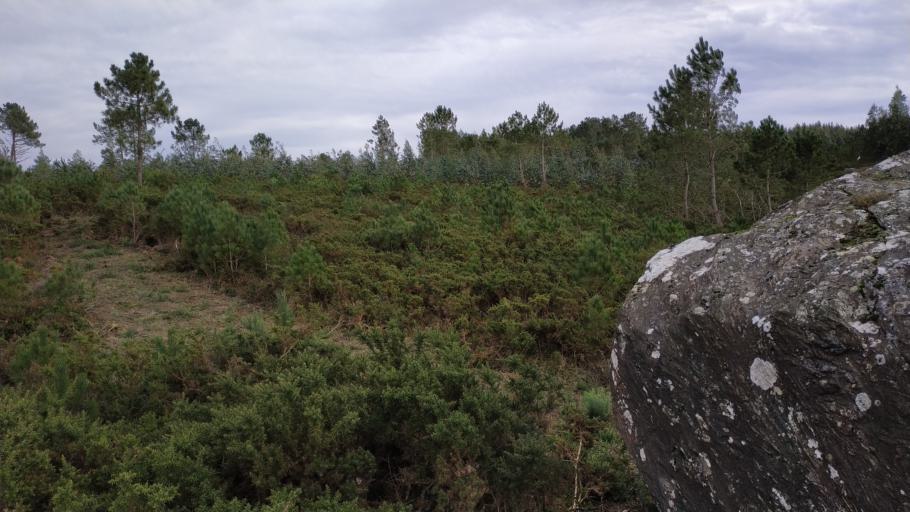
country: ES
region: Galicia
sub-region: Provincia de Pontevedra
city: Silleda
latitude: 42.7731
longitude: -8.1656
